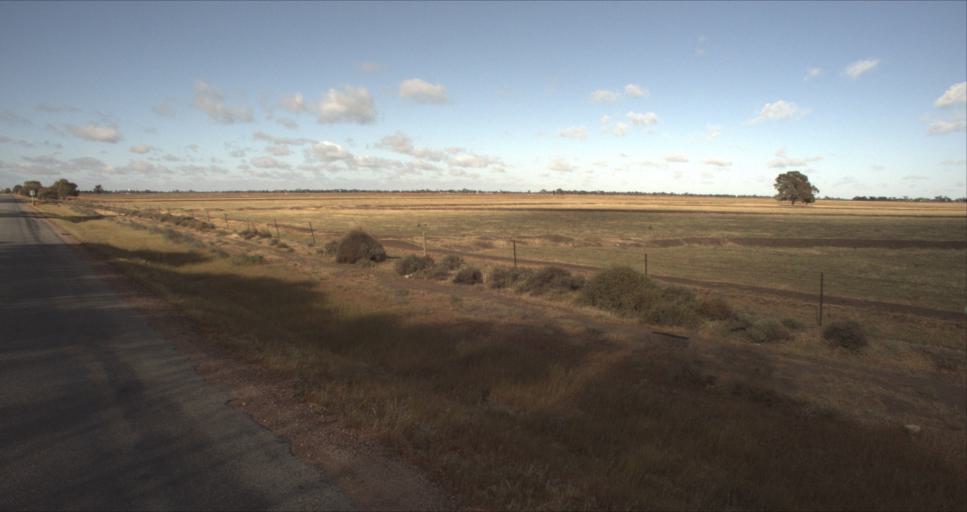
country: AU
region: New South Wales
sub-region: Leeton
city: Leeton
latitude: -34.5050
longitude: 146.3933
